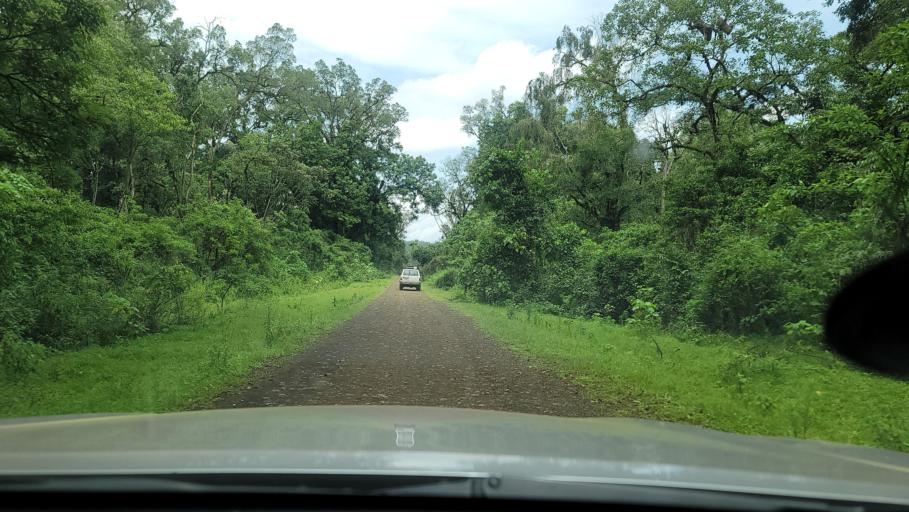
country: ET
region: Southern Nations, Nationalities, and People's Region
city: Bonga
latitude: 7.6527
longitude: 36.2465
